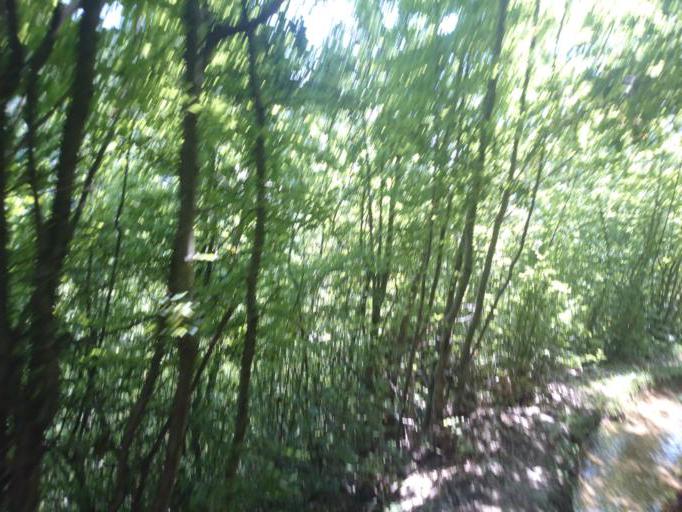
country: AL
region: Diber
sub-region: Rrethi i Dibres
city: Melan
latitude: 41.6223
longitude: 20.4214
